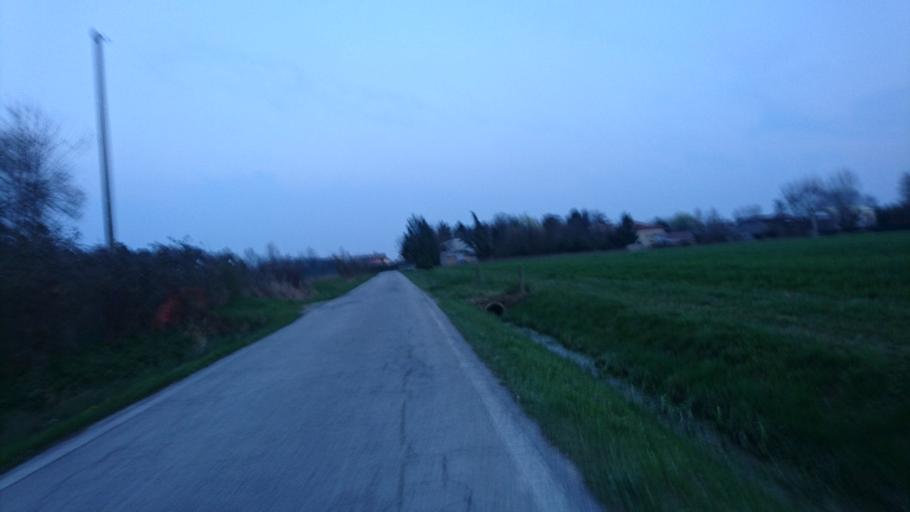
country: IT
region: Veneto
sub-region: Provincia di Padova
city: Saccolongo
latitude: 45.3856
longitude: 11.7562
